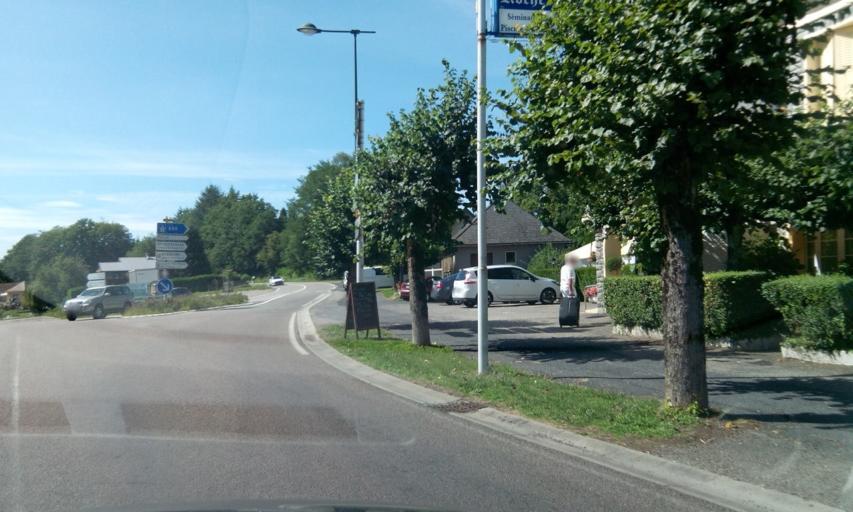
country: FR
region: Limousin
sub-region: Departement de la Correze
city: Beynat
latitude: 45.1358
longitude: 1.7826
